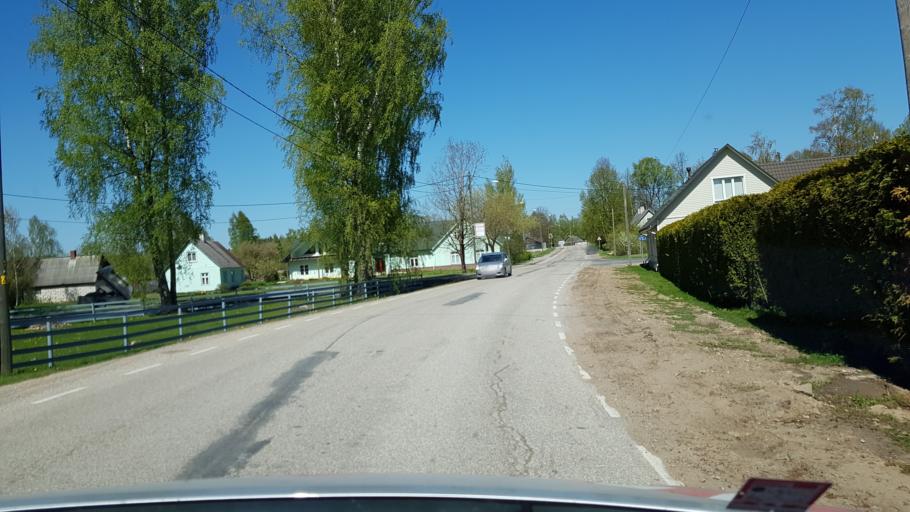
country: EE
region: Vorumaa
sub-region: Antsla vald
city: Vana-Antsla
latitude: 57.8243
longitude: 26.5236
